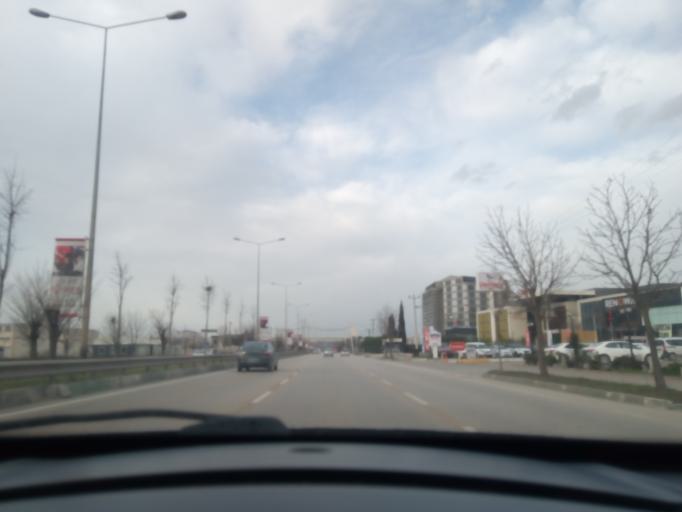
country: TR
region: Bursa
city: Cali
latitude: 40.2144
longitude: 28.9060
